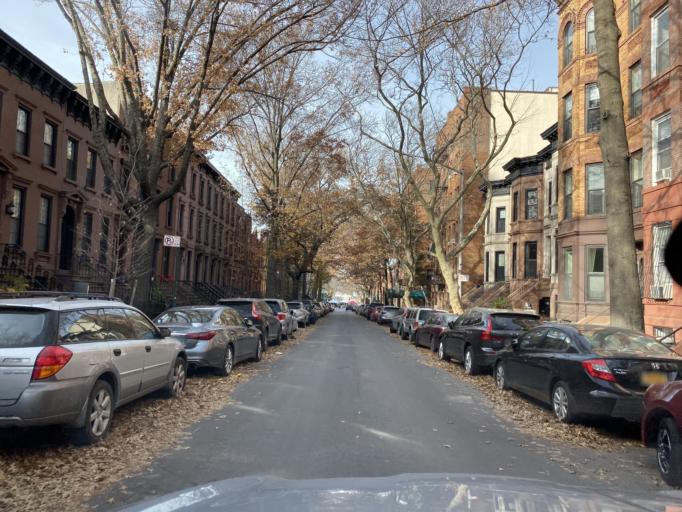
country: US
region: New York
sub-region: Kings County
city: Brooklyn
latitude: 40.6714
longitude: -73.9822
